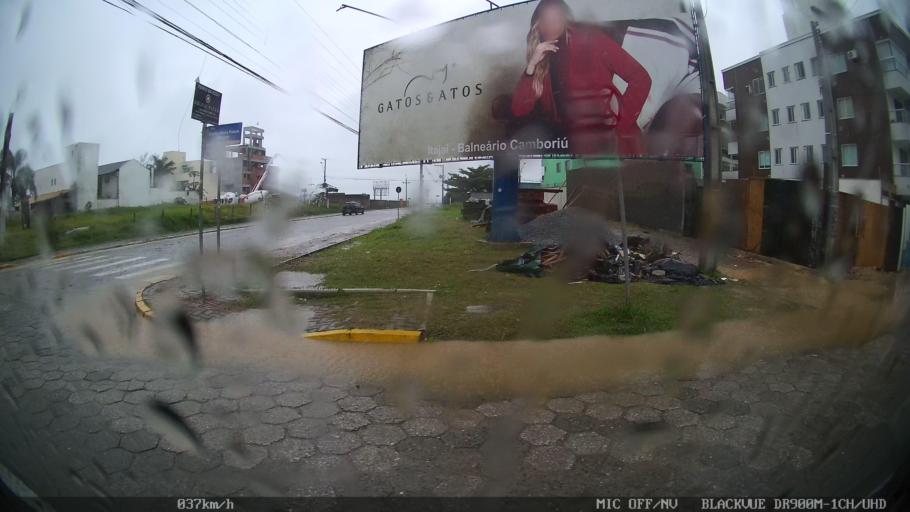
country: BR
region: Santa Catarina
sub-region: Balneario Camboriu
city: Balneario Camboriu
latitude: -26.9484
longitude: -48.6306
